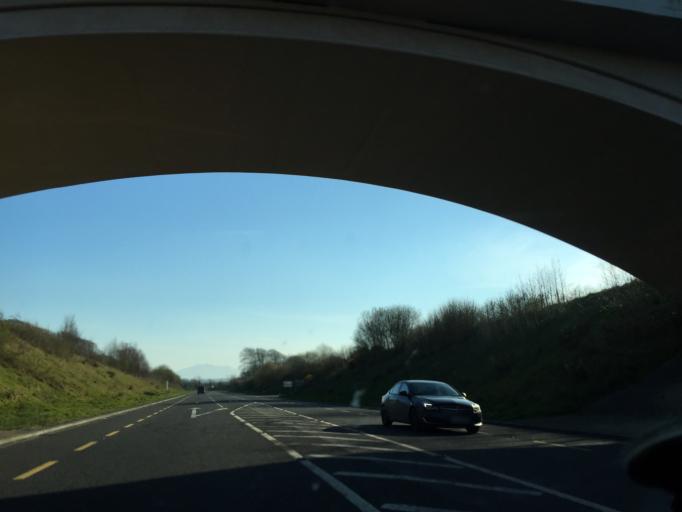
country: IE
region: Munster
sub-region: Ciarrai
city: Castleisland
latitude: 52.2043
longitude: -9.5689
